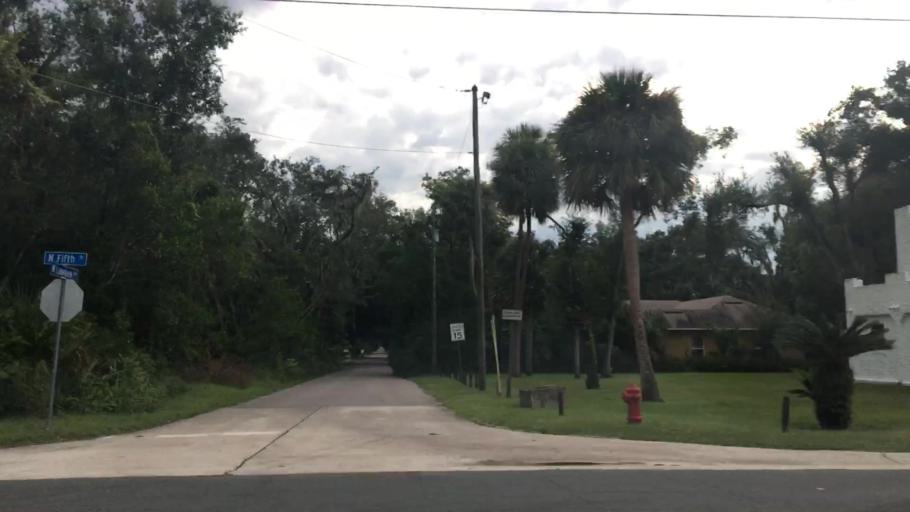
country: US
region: Florida
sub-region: Seminole County
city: Lake Mary
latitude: 28.7581
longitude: -81.3261
